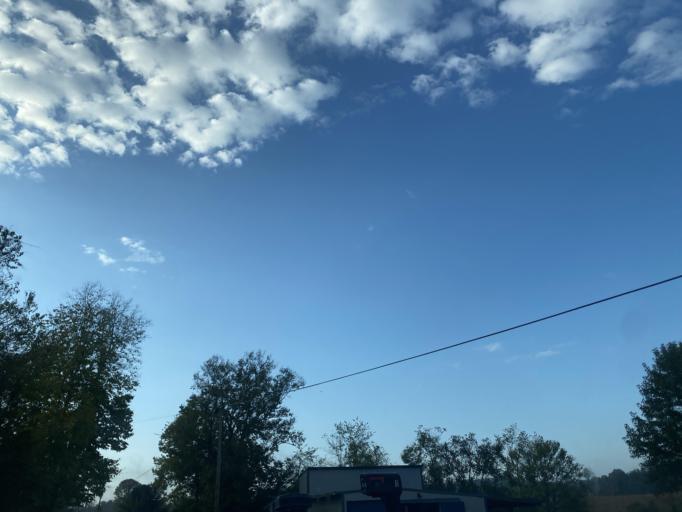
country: US
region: Kentucky
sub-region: Pendleton County
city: Falmouth
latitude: 38.7549
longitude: -84.3395
